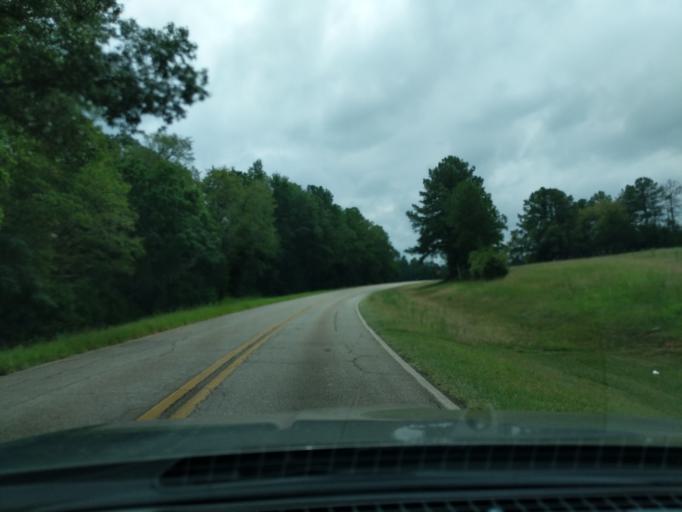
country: US
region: Georgia
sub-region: Columbia County
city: Appling
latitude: 33.5807
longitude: -82.3706
